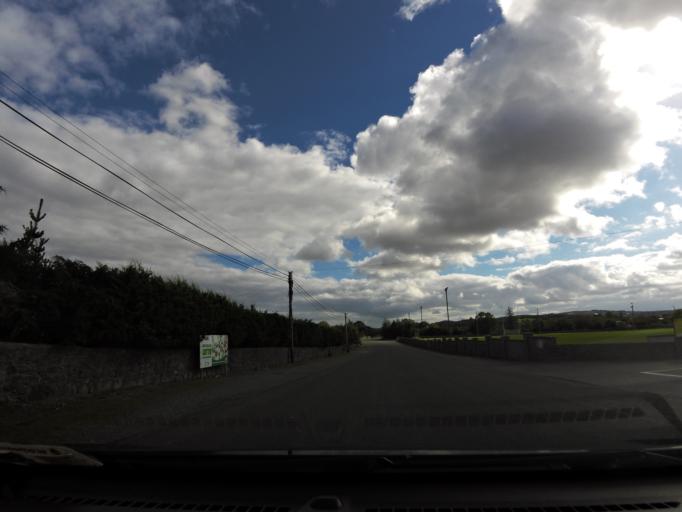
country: IE
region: Connaught
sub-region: County Galway
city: Moycullen
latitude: 53.3596
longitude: -9.1744
